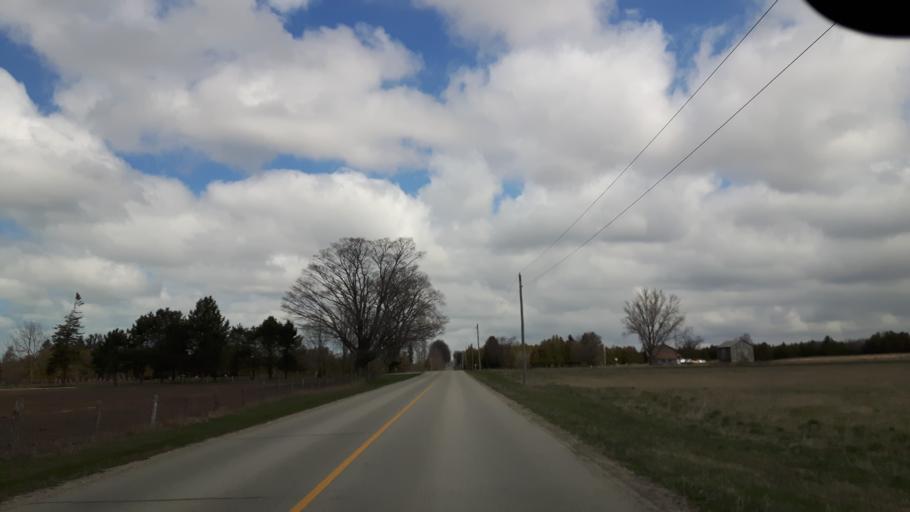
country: CA
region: Ontario
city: Goderich
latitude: 43.6637
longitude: -81.6846
